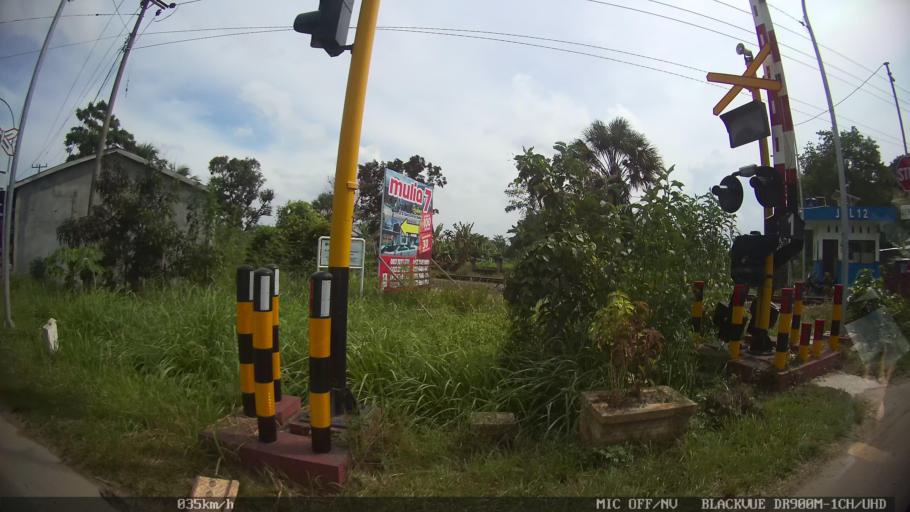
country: ID
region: North Sumatra
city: Percut
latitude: 3.6093
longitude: 98.8503
